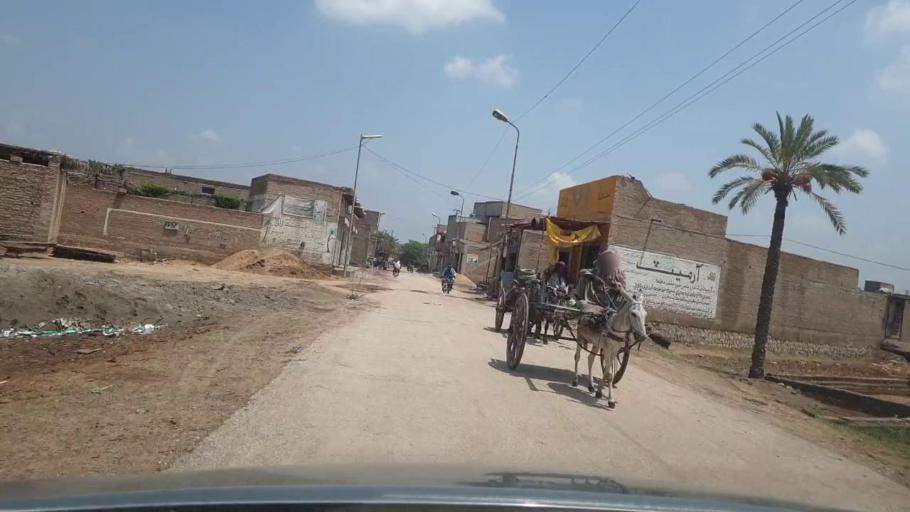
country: PK
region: Sindh
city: Pir jo Goth
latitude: 27.5951
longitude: 68.6116
